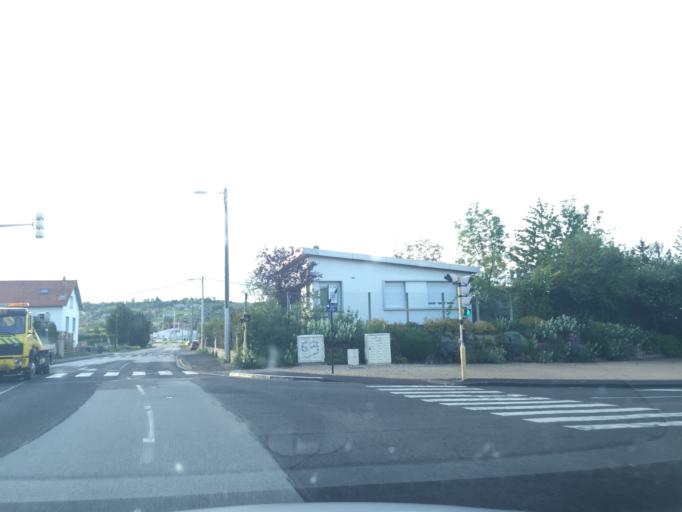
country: FR
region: Auvergne
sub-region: Departement du Puy-de-Dome
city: Riom
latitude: 45.9007
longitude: 3.1039
